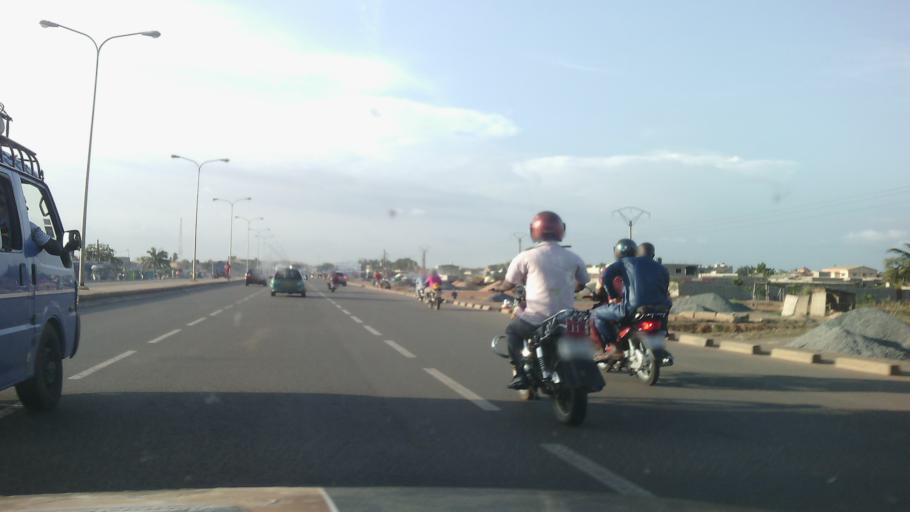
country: TG
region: Maritime
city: Lome
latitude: 6.2467
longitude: 1.2096
